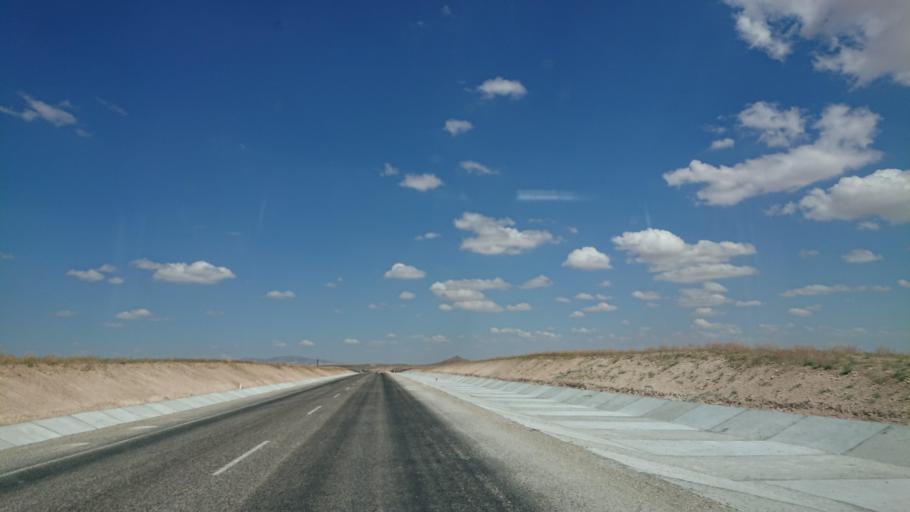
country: TR
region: Kirsehir
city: Kirsehir
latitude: 39.1227
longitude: 34.0016
